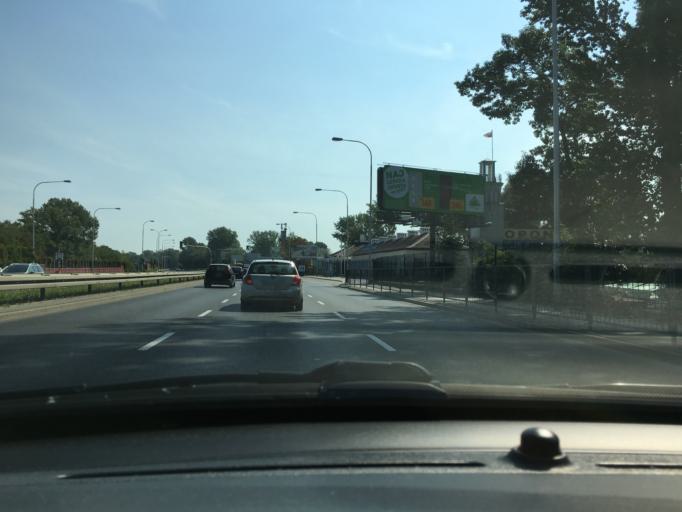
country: PL
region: Masovian Voivodeship
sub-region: Warszawa
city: Praga Poludnie
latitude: 52.2224
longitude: 21.0625
